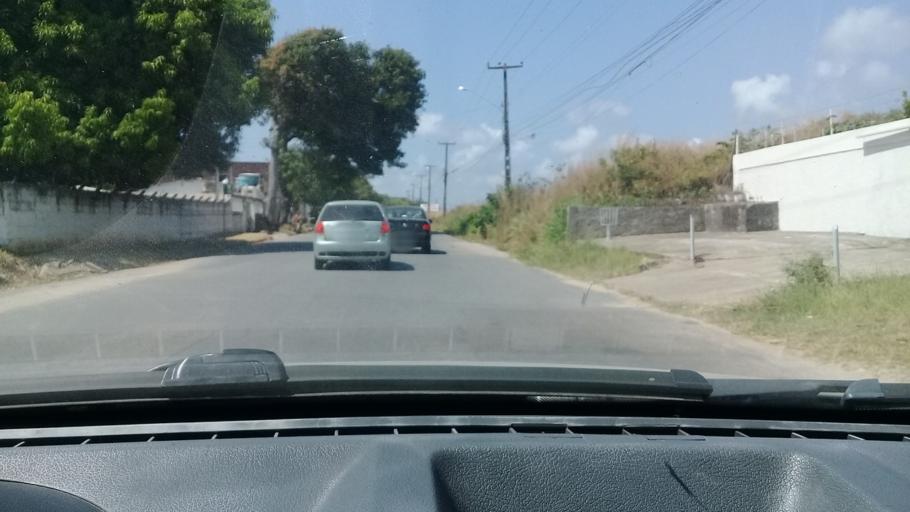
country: BR
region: Pernambuco
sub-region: Itamaraca
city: Itamaraca
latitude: -7.7793
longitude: -34.8361
